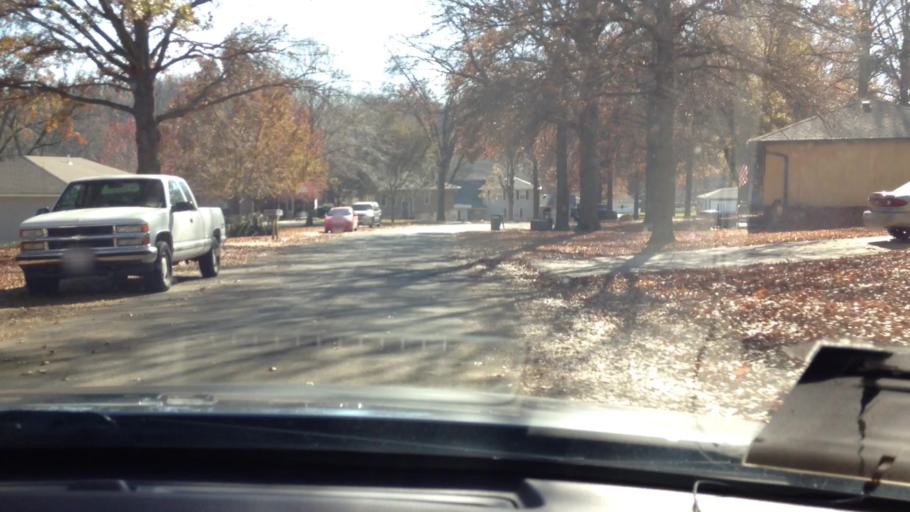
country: US
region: Missouri
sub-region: Platte County
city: Weston
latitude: 39.4119
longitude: -94.8873
